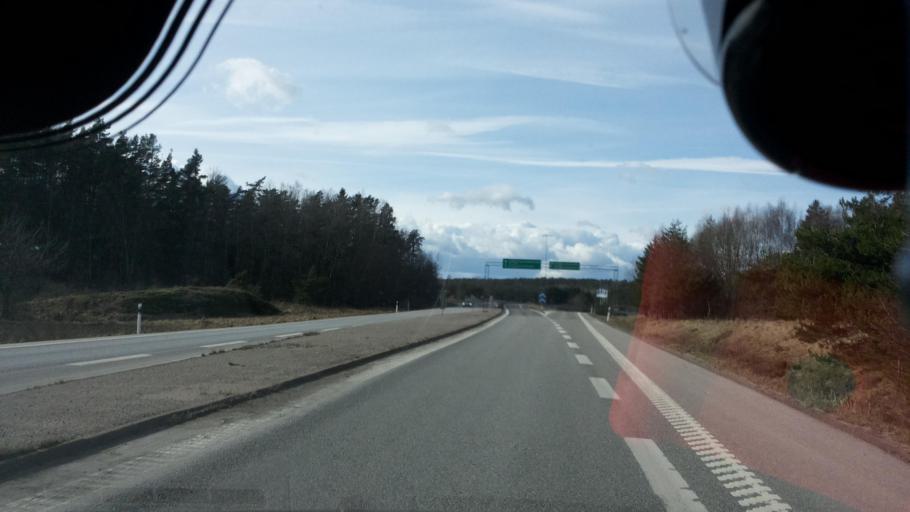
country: SE
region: Soedermanland
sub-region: Trosa Kommun
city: Vagnharad
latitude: 58.9588
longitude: 17.4904
